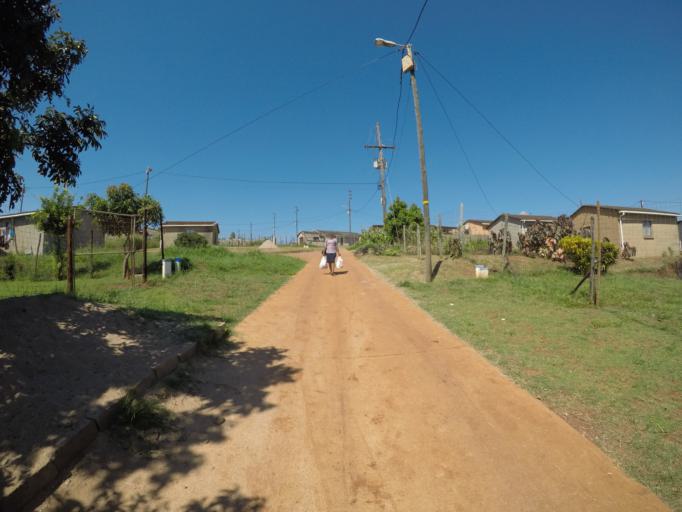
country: ZA
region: KwaZulu-Natal
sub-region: uThungulu District Municipality
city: Empangeni
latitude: -28.7719
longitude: 31.8761
